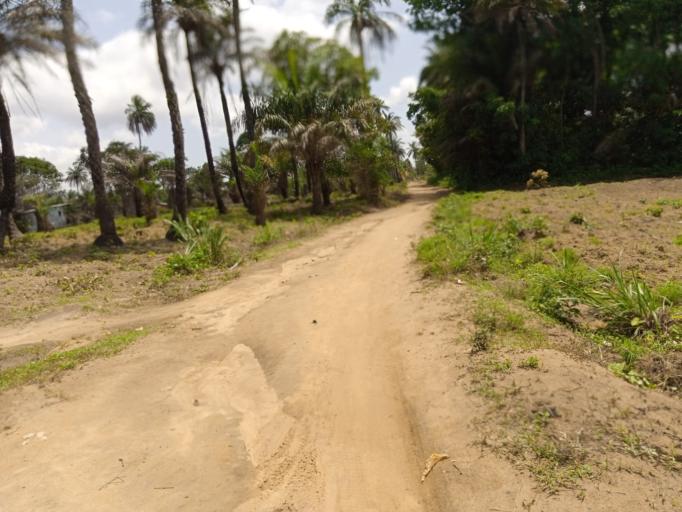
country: SL
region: Western Area
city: Waterloo
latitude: 8.3213
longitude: -13.0111
